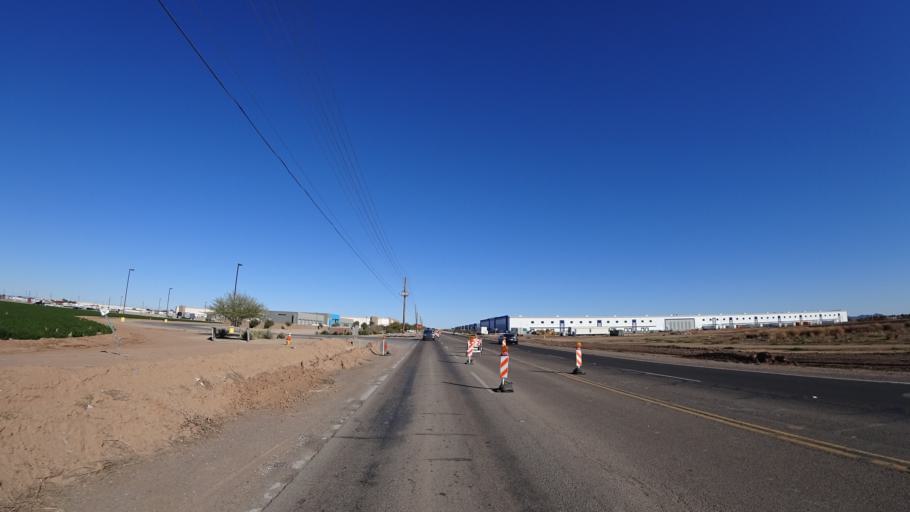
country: US
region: Arizona
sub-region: Maricopa County
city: Tolleson
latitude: 33.4361
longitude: -112.2528
